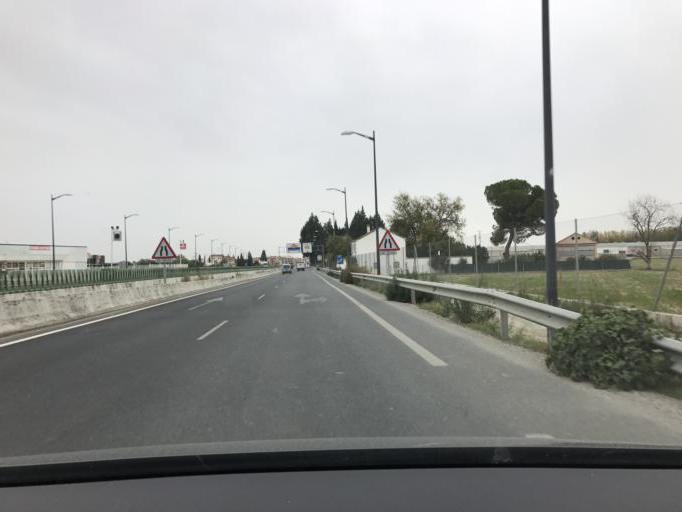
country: ES
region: Andalusia
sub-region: Provincia de Granada
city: Atarfe
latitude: 37.1931
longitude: -3.7013
